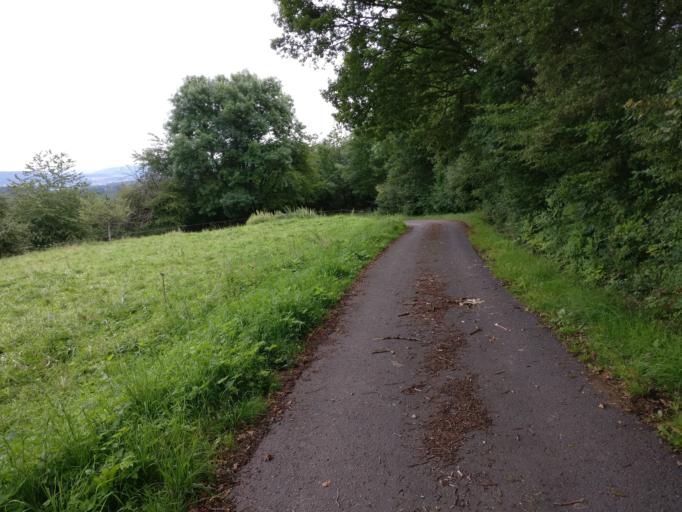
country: DE
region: Hesse
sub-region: Regierungsbezirk Giessen
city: Greifenstein
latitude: 50.6196
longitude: 8.2978
